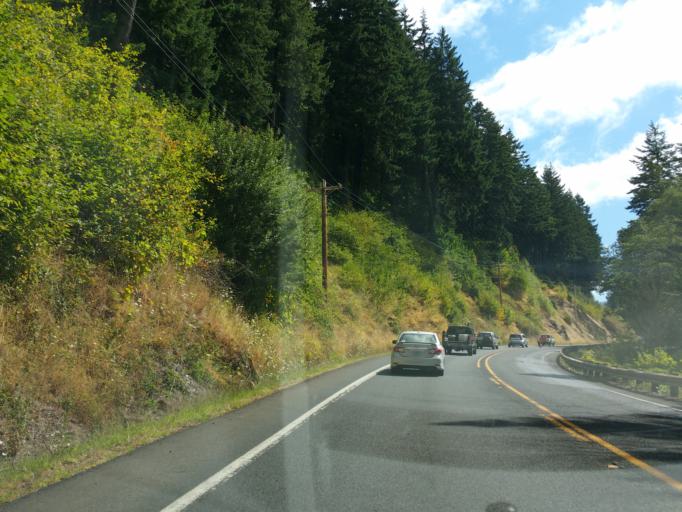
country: US
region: Oregon
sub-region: Hood River County
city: Cascade Locks
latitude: 45.6025
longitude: -122.1080
